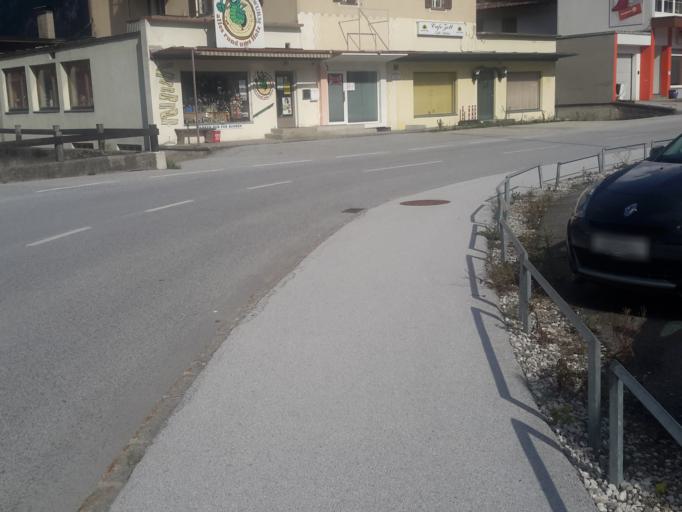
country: AT
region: Tyrol
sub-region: Politischer Bezirk Kufstein
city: Kufstein
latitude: 47.5867
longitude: 12.1624
